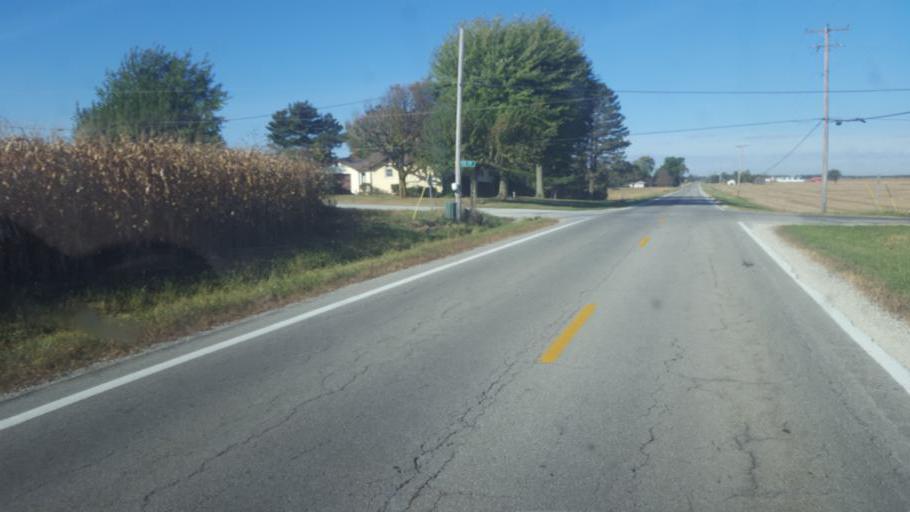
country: US
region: Ohio
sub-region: Marion County
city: Marion
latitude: 40.6878
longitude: -83.1681
